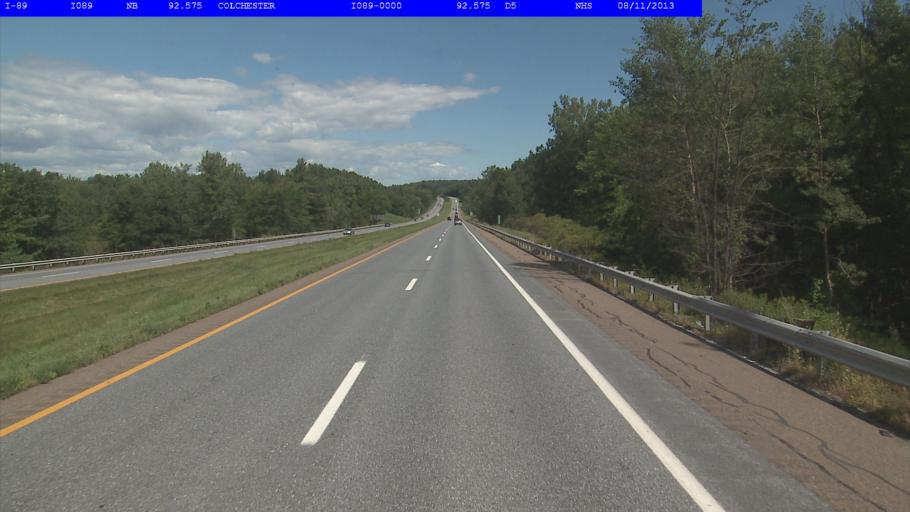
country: US
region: Vermont
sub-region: Chittenden County
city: Winooski
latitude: 44.5178
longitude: -73.1920
